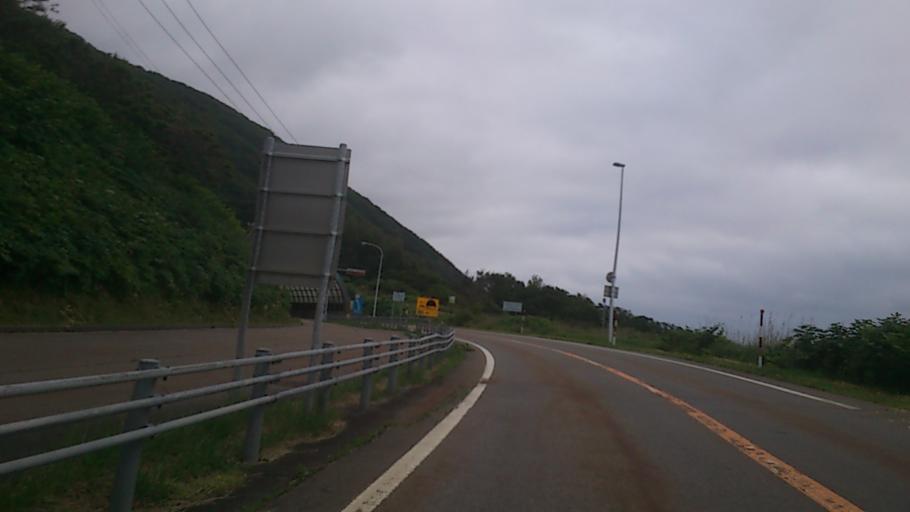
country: JP
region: Hokkaido
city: Kamiiso
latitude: 41.6576
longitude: 140.0055
